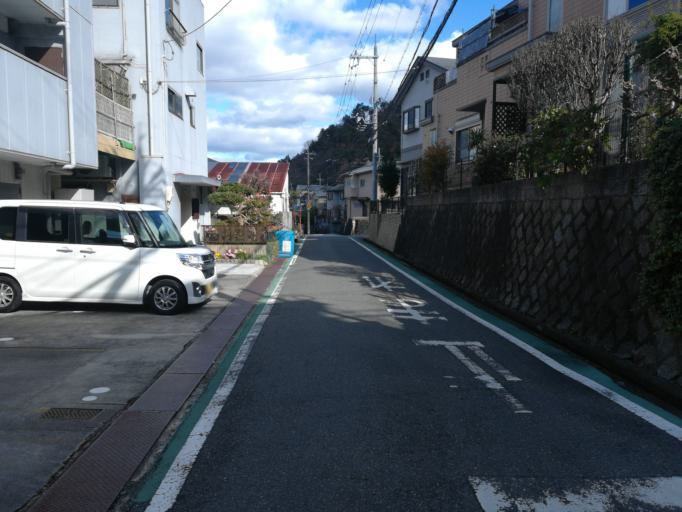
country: JP
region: Kyoto
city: Kameoka
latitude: 34.9967
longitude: 135.5549
